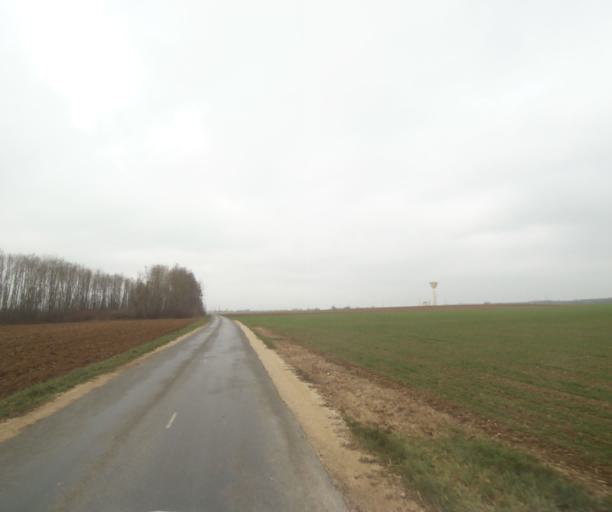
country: FR
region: Champagne-Ardenne
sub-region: Departement de la Haute-Marne
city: Villiers-en-Lieu
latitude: 48.6841
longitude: 4.8258
